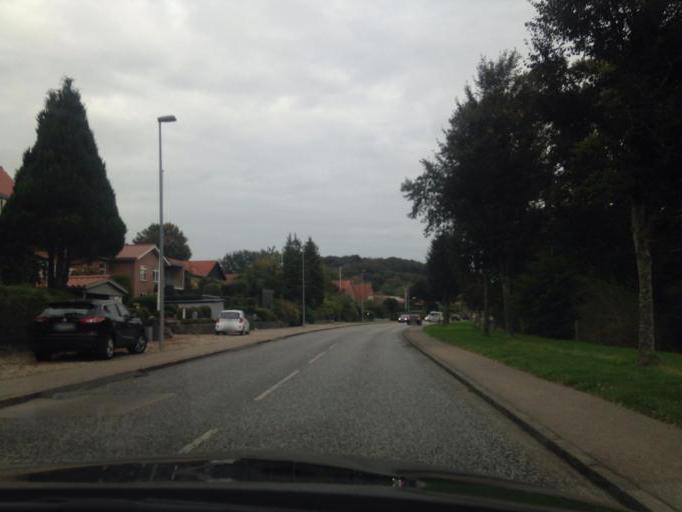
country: DK
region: South Denmark
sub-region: Haderslev Kommune
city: Haderslev
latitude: 55.2455
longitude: 9.4494
